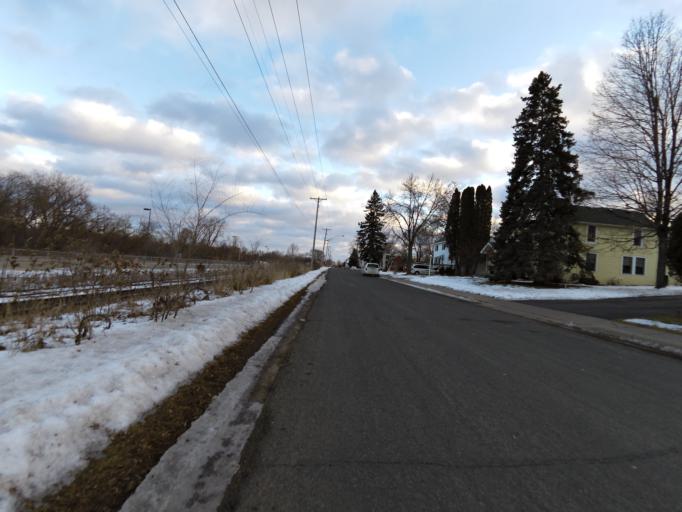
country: US
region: Minnesota
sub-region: Washington County
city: Bayport
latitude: 45.0198
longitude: -92.7773
